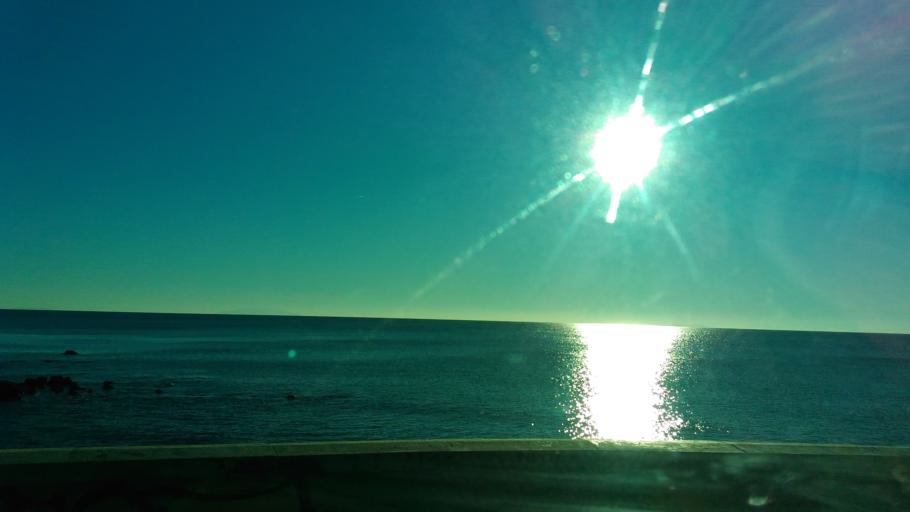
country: IT
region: Tuscany
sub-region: Provincia di Livorno
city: Quercianella
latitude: 43.4565
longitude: 10.3682
